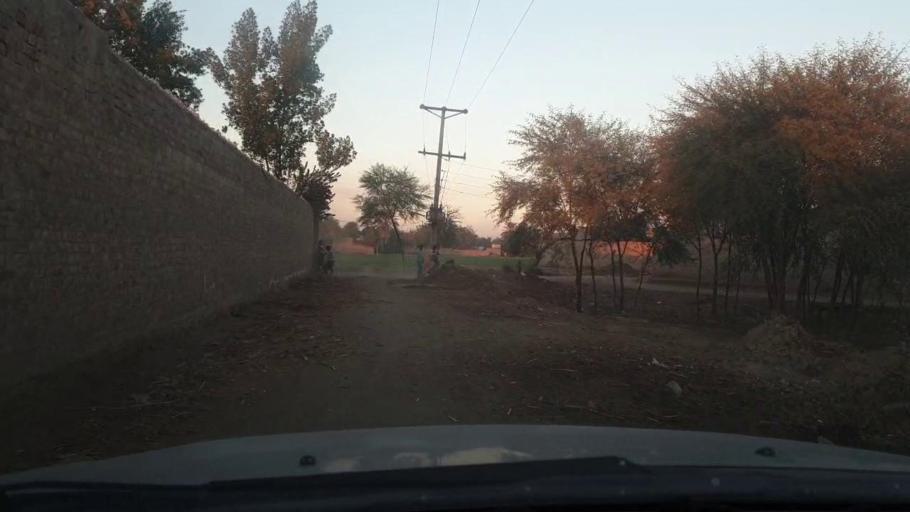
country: PK
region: Sindh
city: Ghotki
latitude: 27.9744
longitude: 69.2578
